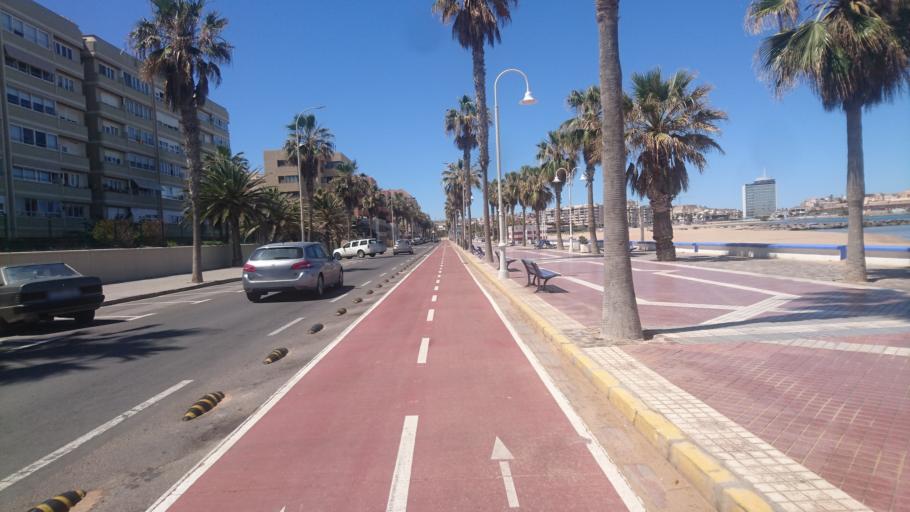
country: ES
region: Melilla
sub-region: Melilla
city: Melilla
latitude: 35.2814
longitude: -2.9374
